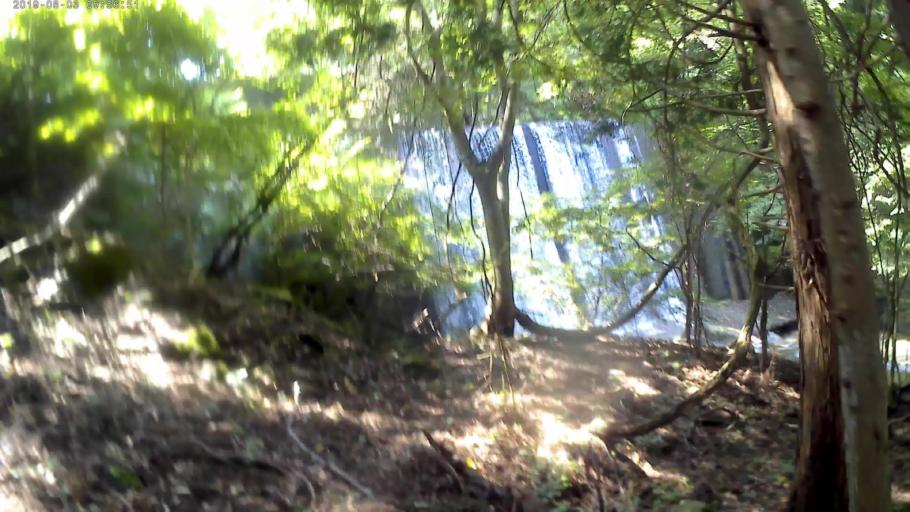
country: JP
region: Yamanashi
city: Enzan
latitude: 35.6322
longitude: 138.7692
